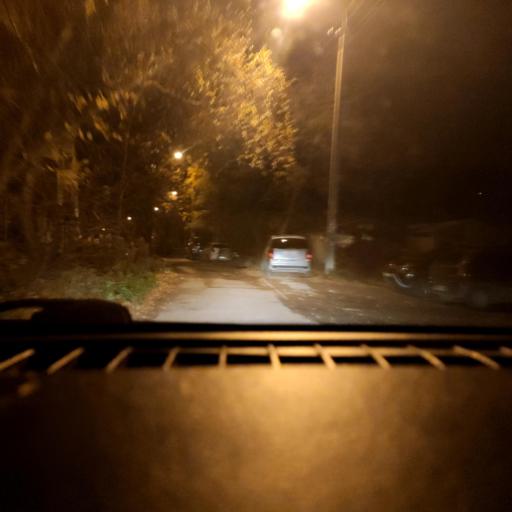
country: RU
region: Perm
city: Perm
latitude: 58.0002
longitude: 56.2154
